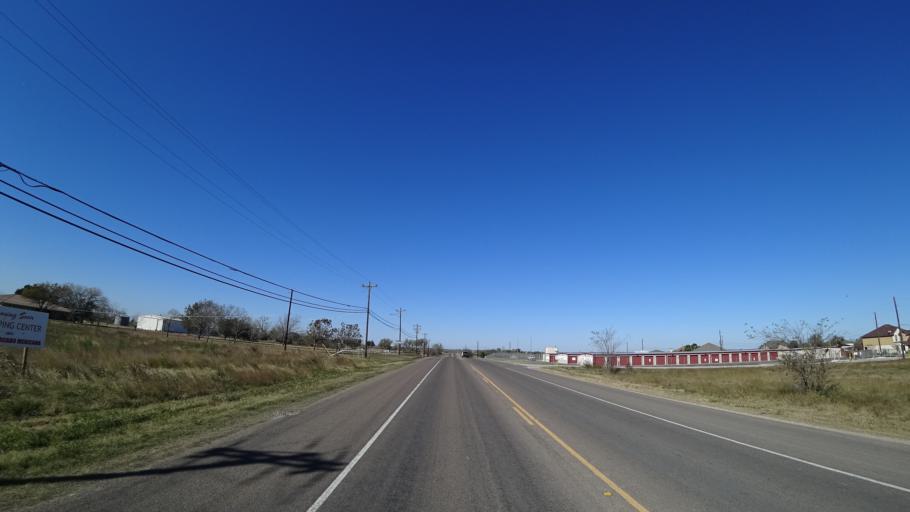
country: US
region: Texas
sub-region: Travis County
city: Garfield
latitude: 30.0964
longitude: -97.6018
